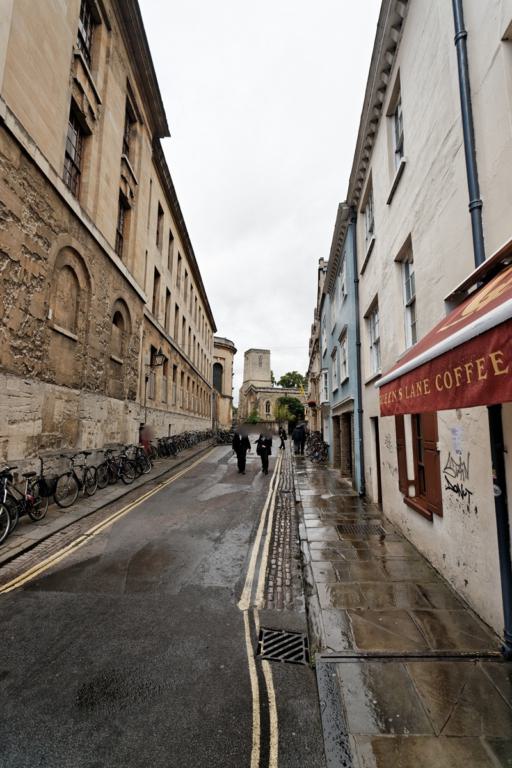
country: GB
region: England
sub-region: Oxfordshire
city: Oxford
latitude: 51.7528
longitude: -1.2505
